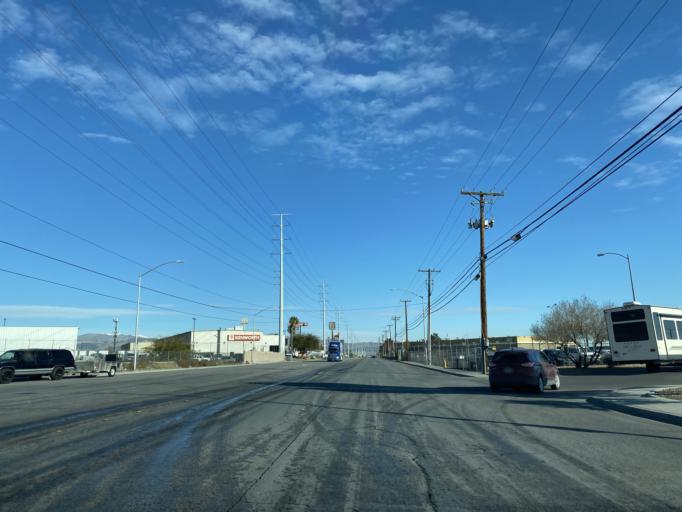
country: US
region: Nevada
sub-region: Clark County
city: North Las Vegas
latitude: 36.2138
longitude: -115.1300
